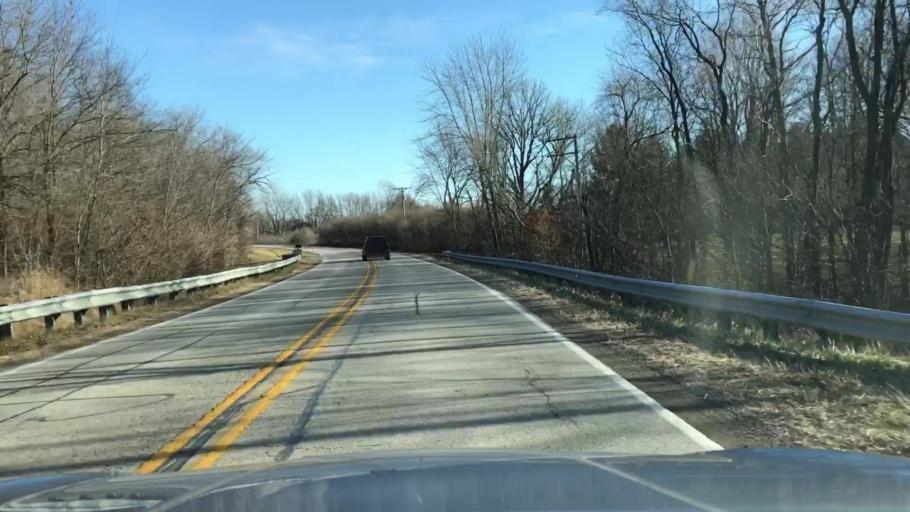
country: US
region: Illinois
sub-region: McLean County
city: Lexington
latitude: 40.6459
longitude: -88.8372
